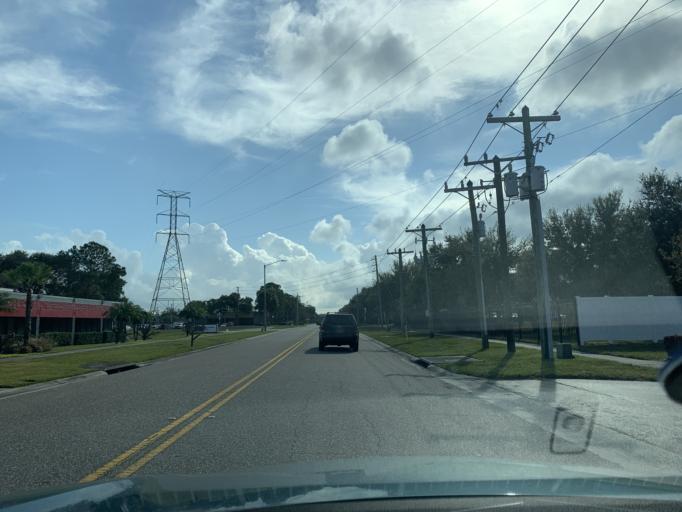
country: US
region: Florida
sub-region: Pinellas County
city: South Highpoint
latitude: 27.9042
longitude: -82.7127
